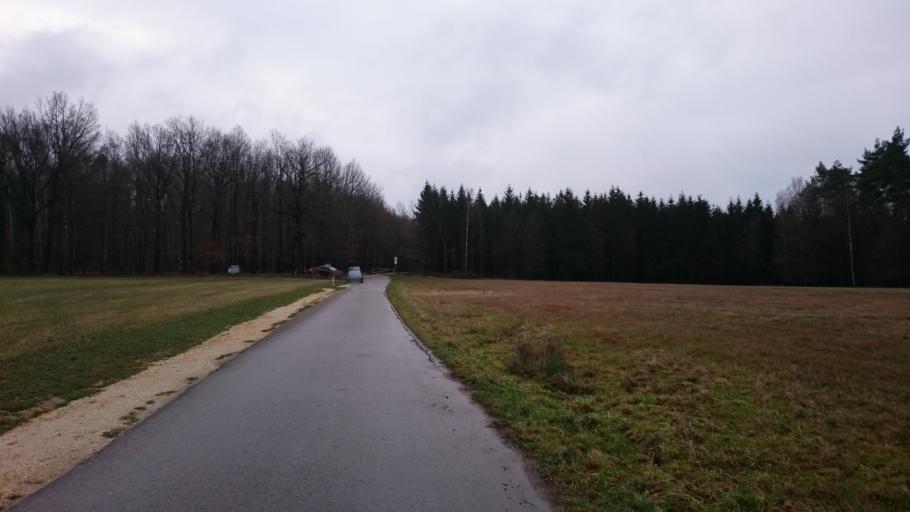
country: DE
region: Saxony
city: Glauchau
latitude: 50.7861
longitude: 12.5574
